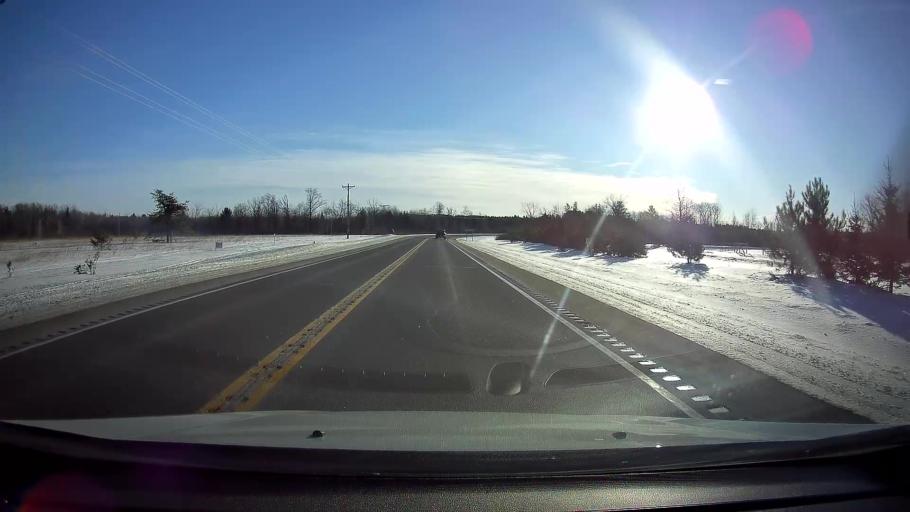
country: US
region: Wisconsin
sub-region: Sawyer County
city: Hayward
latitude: 45.9962
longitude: -91.5969
